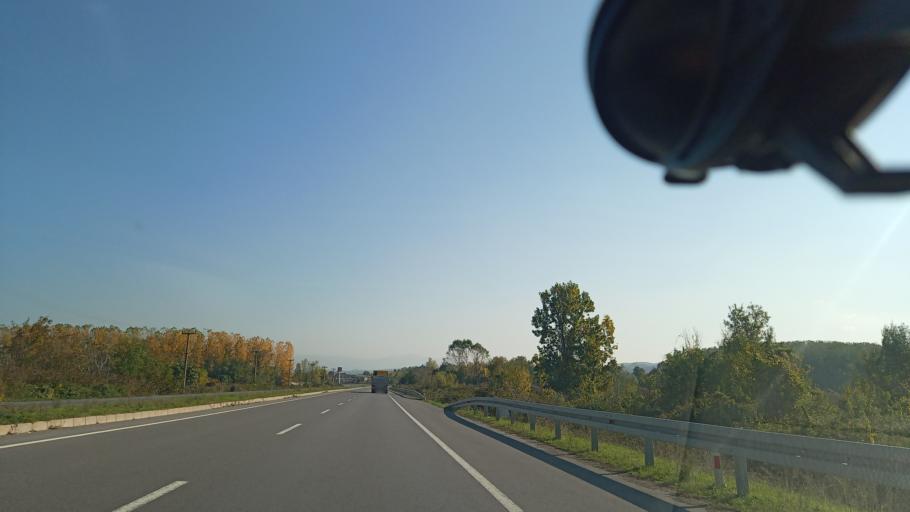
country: TR
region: Sakarya
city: Karasu
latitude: 41.0721
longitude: 30.7913
